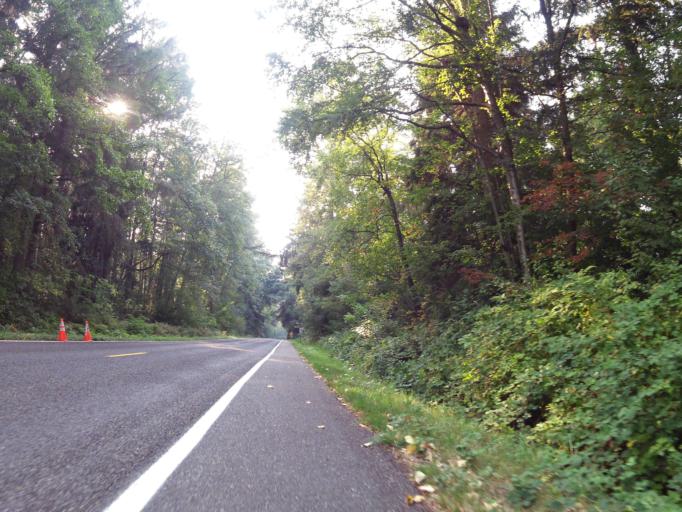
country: US
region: Washington
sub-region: Whatcom County
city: Birch Bay
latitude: 48.9033
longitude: -122.7576
